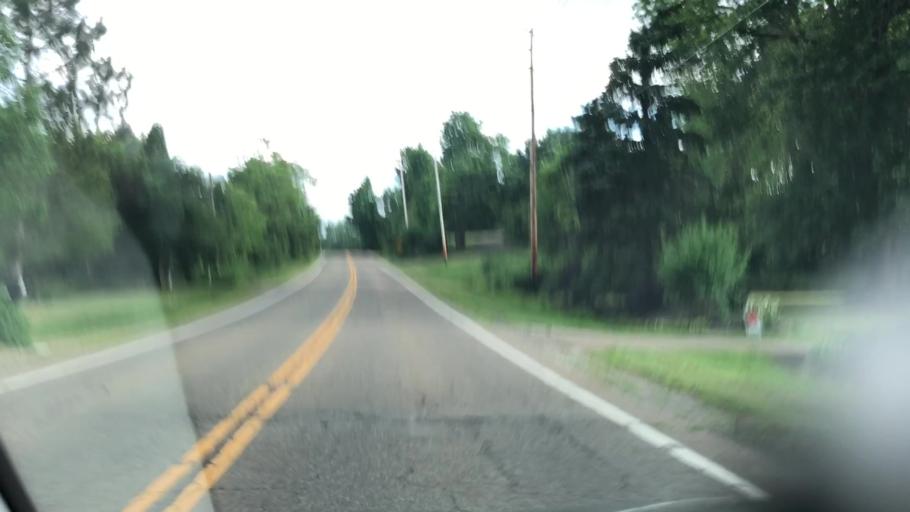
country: US
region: Ohio
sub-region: Summit County
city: Norton
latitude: 41.0645
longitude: -81.6383
